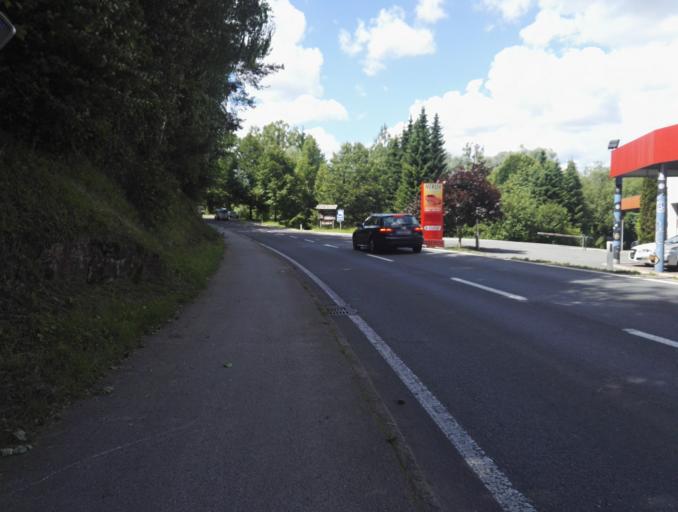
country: AT
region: Styria
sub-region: Politischer Bezirk Graz-Umgebung
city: Gratkorn
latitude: 47.1177
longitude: 15.3529
